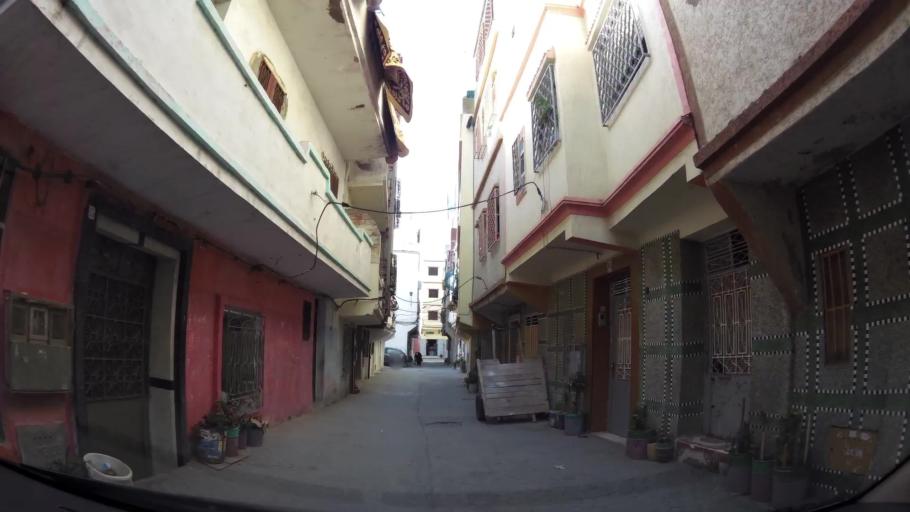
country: MA
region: Tanger-Tetouan
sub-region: Tanger-Assilah
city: Tangier
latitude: 35.7596
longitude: -5.7874
